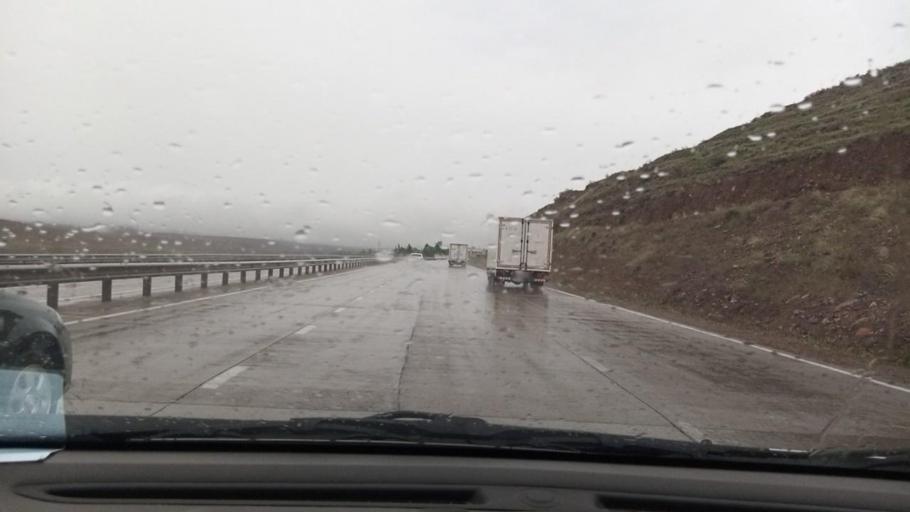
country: UZ
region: Namangan
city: Pop Shahri
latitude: 40.9255
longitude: 70.7236
